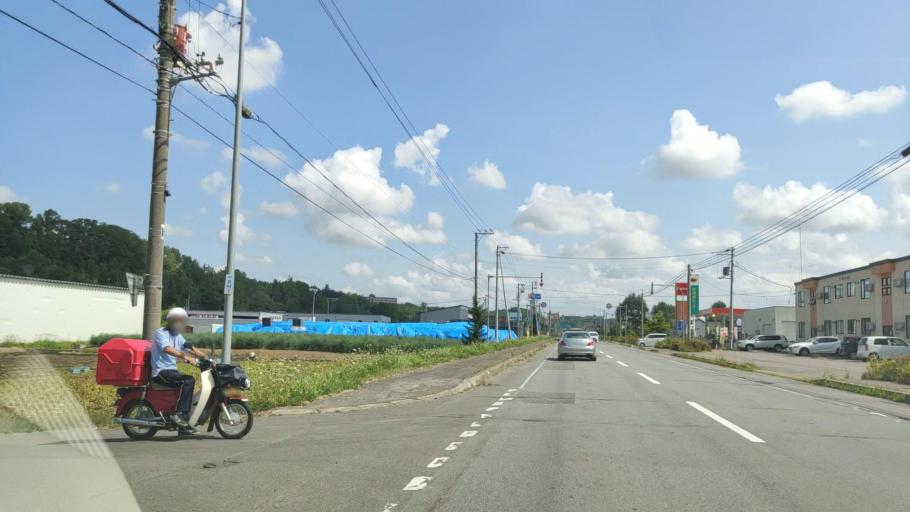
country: JP
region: Hokkaido
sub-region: Asahikawa-shi
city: Asahikawa
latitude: 43.5927
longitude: 142.4566
